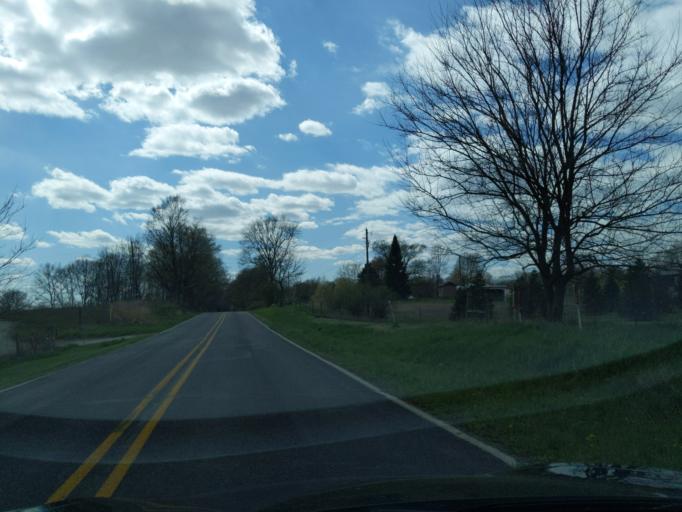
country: US
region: Michigan
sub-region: Ingham County
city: Leslie
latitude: 42.3935
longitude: -84.5275
